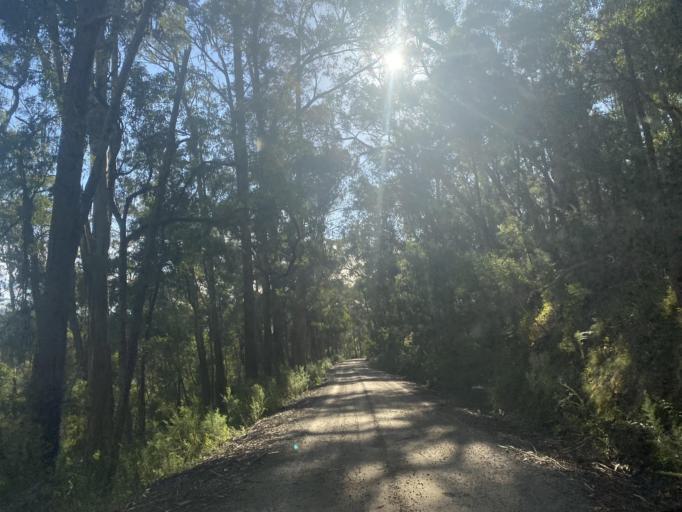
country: AU
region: Victoria
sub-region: Mansfield
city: Mansfield
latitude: -36.8324
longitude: 146.1673
